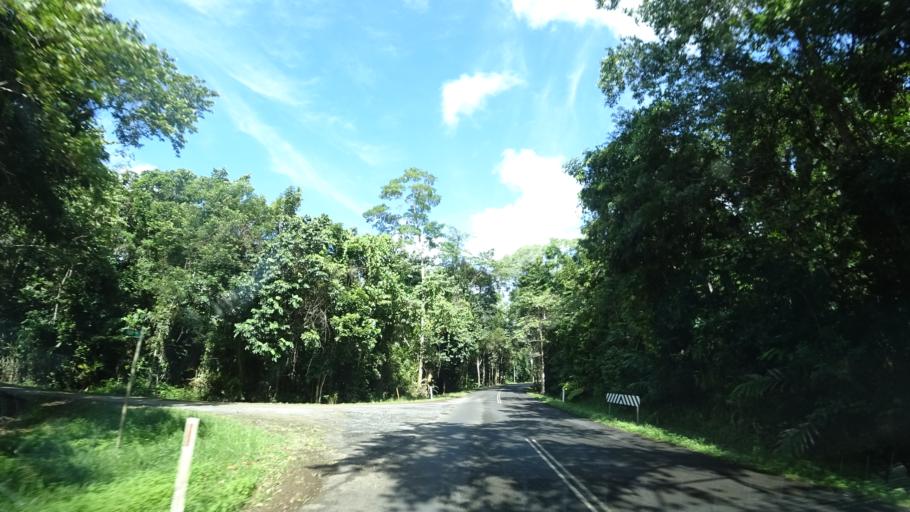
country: AU
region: Queensland
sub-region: Cairns
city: Port Douglas
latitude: -16.2038
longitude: 145.4111
